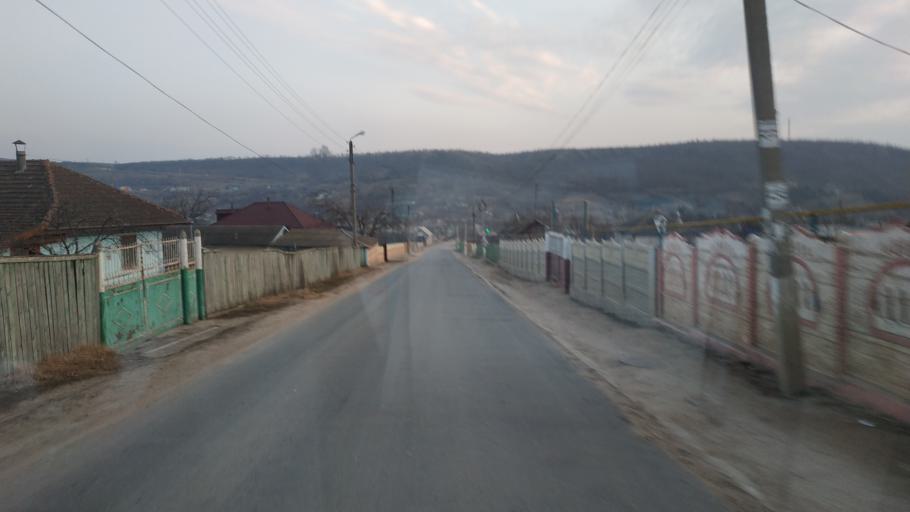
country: MD
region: Hincesti
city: Dancu
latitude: 46.6684
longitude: 28.3280
